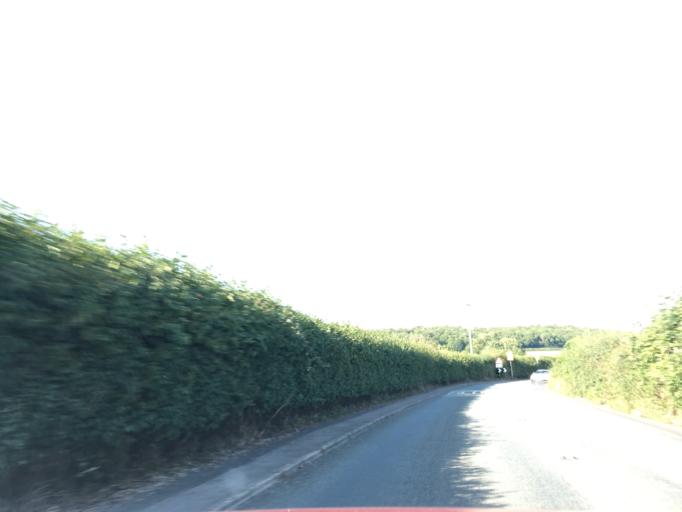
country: GB
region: England
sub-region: Somerset
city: Mendip
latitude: 51.2210
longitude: -2.6123
